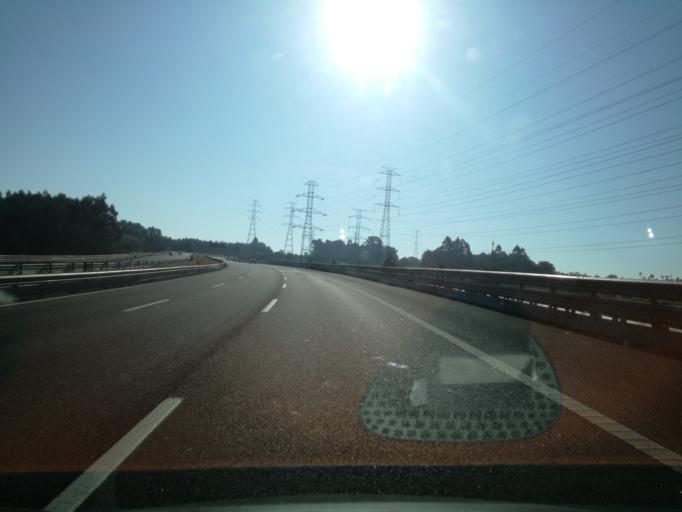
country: PT
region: Porto
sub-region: Maia
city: Nogueira
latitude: 41.2378
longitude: -8.5861
